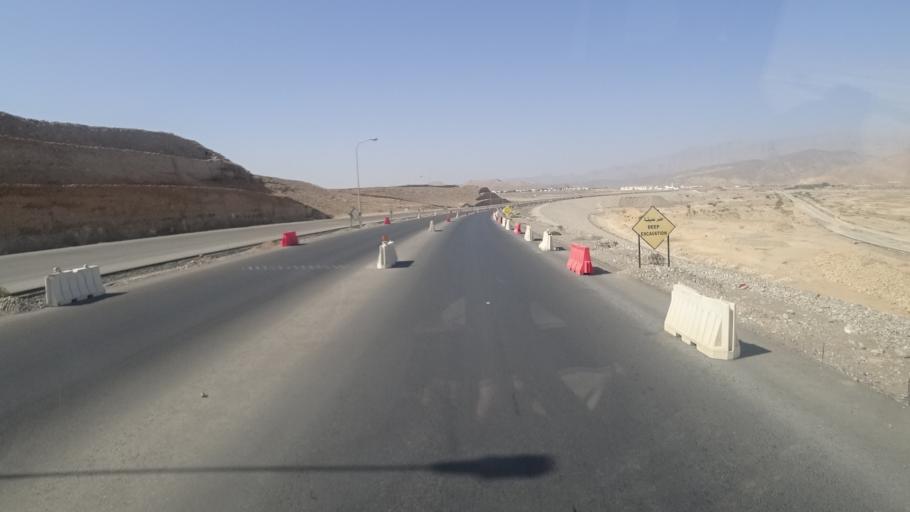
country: OM
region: Ash Sharqiyah
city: Sur
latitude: 22.5200
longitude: 59.4621
